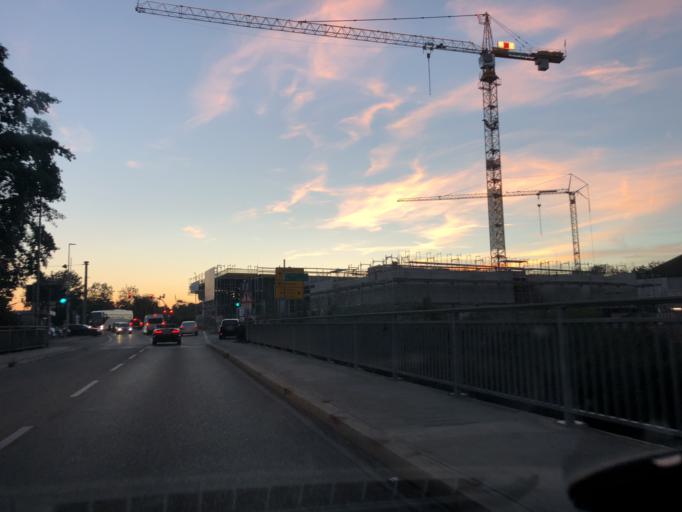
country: DE
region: Baden-Wuerttemberg
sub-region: Regierungsbezirk Stuttgart
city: Stuttgart Muehlhausen
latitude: 48.8722
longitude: 9.2749
